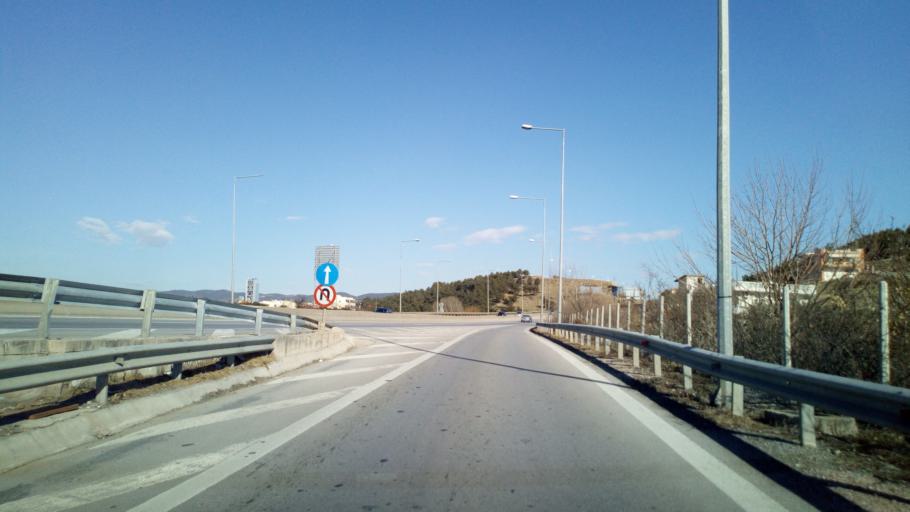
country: GR
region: Central Macedonia
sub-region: Nomos Thessalonikis
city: Efkarpia
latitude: 40.6833
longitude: 22.9573
